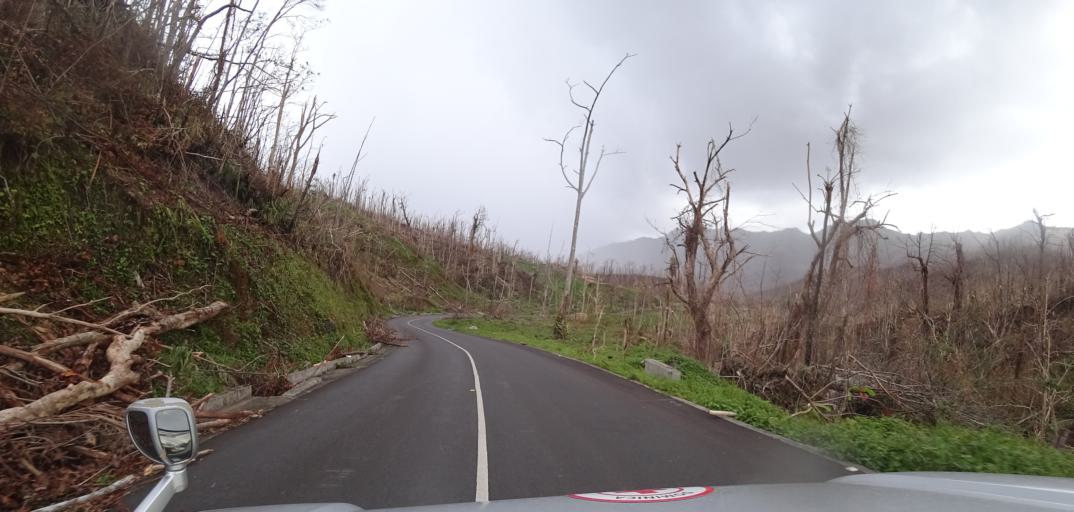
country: DM
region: Saint David
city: Castle Bruce
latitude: 15.4751
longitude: -61.2987
